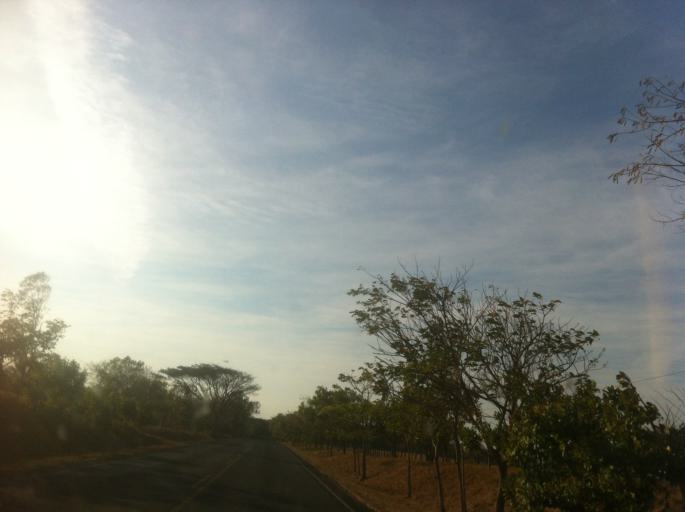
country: NI
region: Rivas
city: San Jorge
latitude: 11.3158
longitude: -85.7096
